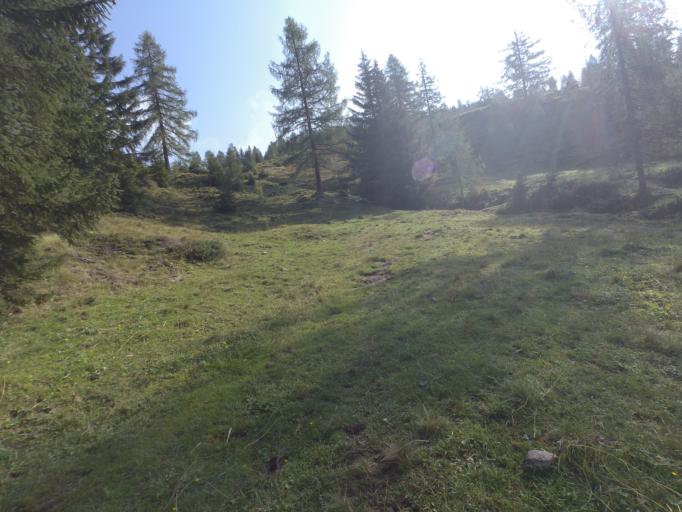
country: AT
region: Salzburg
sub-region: Politischer Bezirk Sankt Johann im Pongau
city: Kleinarl
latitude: 47.2641
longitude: 13.2675
